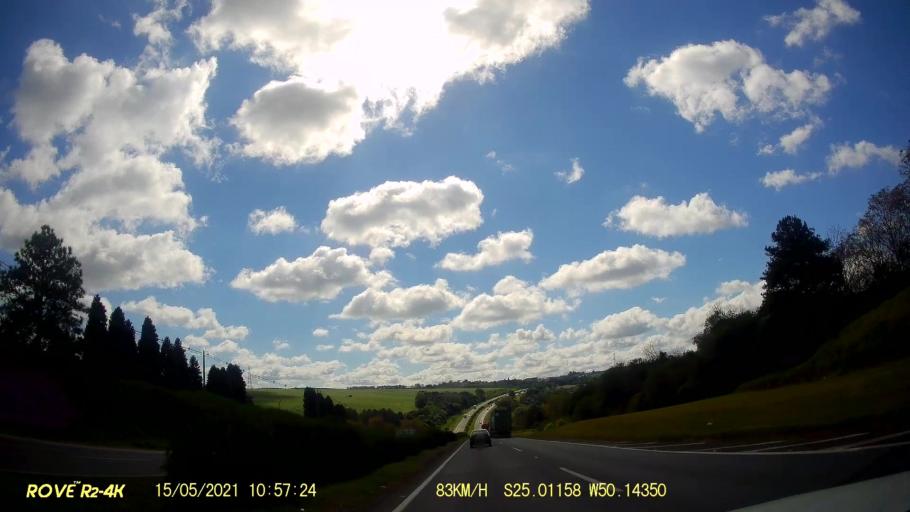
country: BR
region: Parana
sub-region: Carambei
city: Carambei
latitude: -25.0117
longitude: -50.1436
